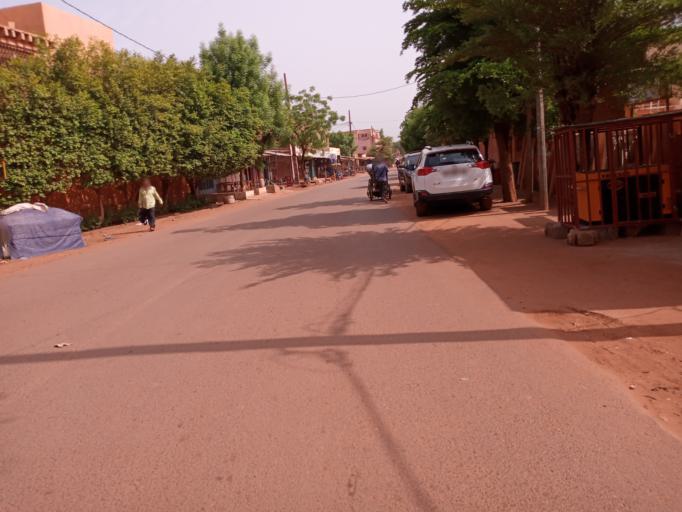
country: ML
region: Bamako
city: Bamako
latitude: 12.6066
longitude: -7.9517
